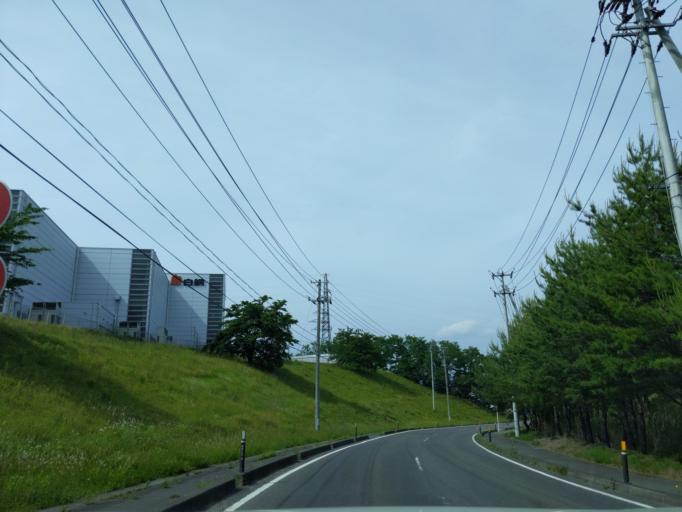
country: JP
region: Fukushima
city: Koriyama
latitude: 37.4502
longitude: 140.3100
